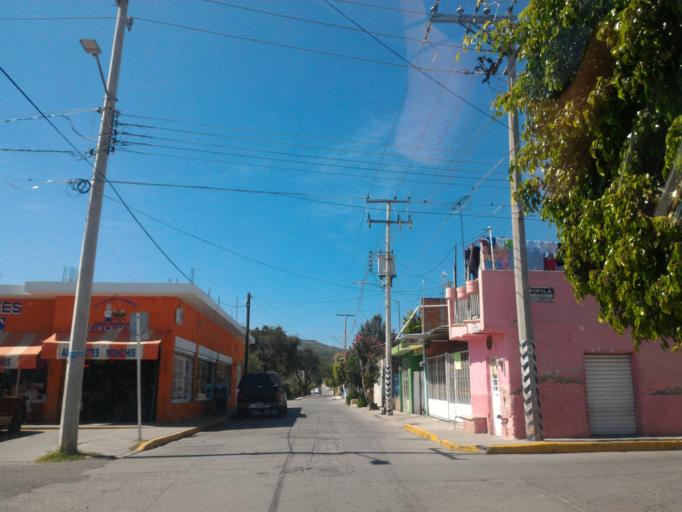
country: MX
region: Guanajuato
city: San Francisco del Rincon
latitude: 21.0327
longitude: -101.8820
